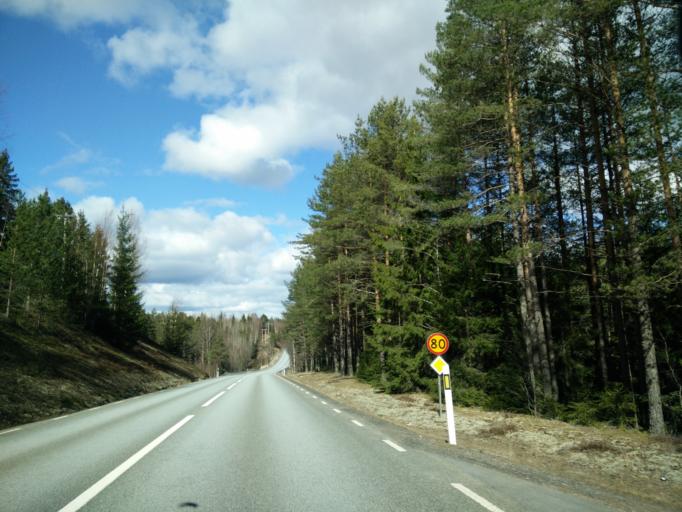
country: SE
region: Vaermland
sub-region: Munkfors Kommun
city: Munkfors
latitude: 59.9192
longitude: 13.5721
